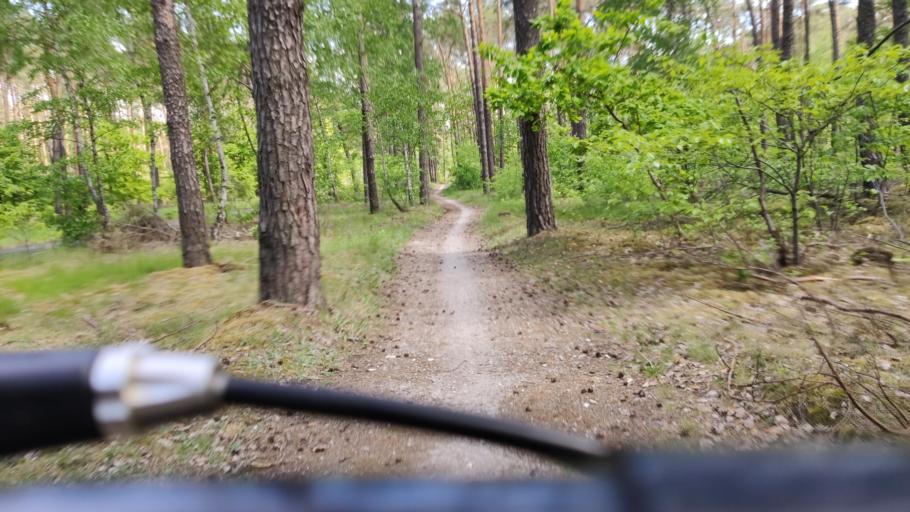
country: PL
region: Kujawsko-Pomorskie
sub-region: Wloclawek
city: Wloclawek
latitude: 52.6359
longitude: 19.1189
